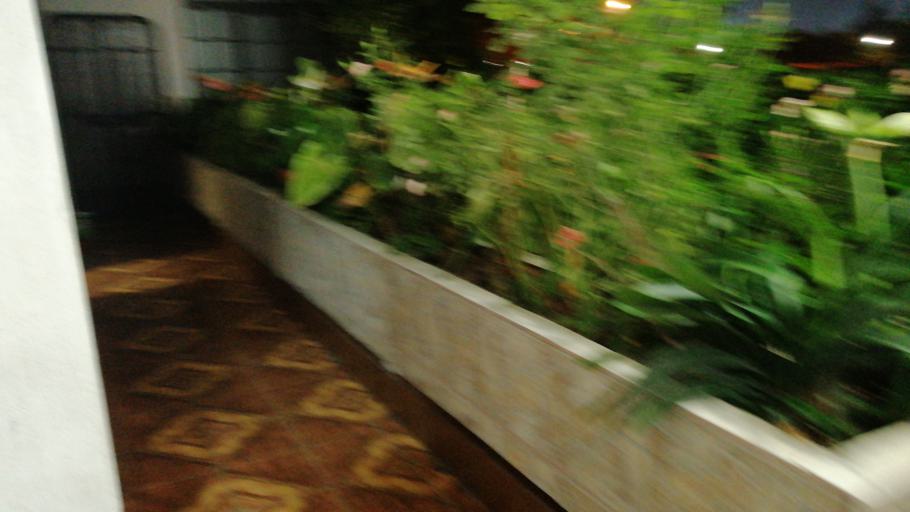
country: GT
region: Guatemala
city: Amatitlan
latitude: 14.4727
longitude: -90.6324
